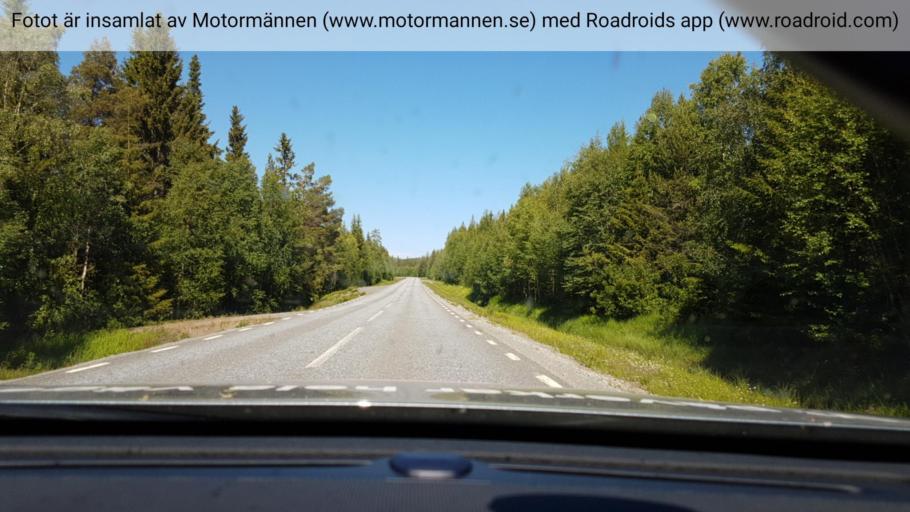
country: SE
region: Vaesterbotten
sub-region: Vilhelmina Kommun
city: Sjoberg
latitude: 64.8612
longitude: 15.8960
